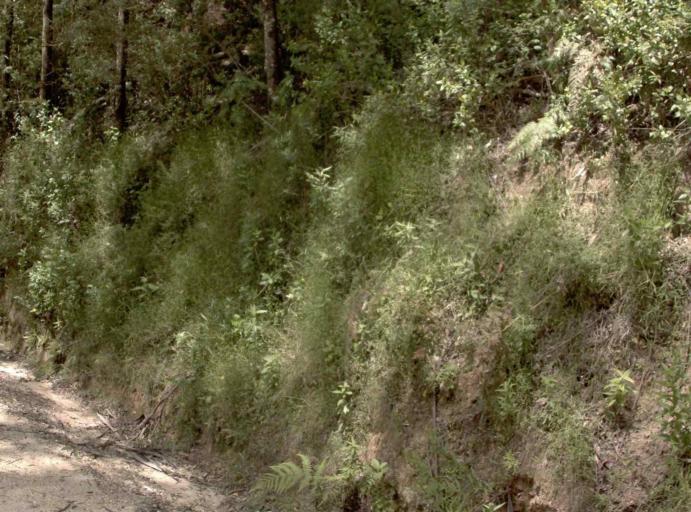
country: AU
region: Victoria
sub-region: Latrobe
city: Morwell
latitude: -38.4381
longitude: 146.5275
